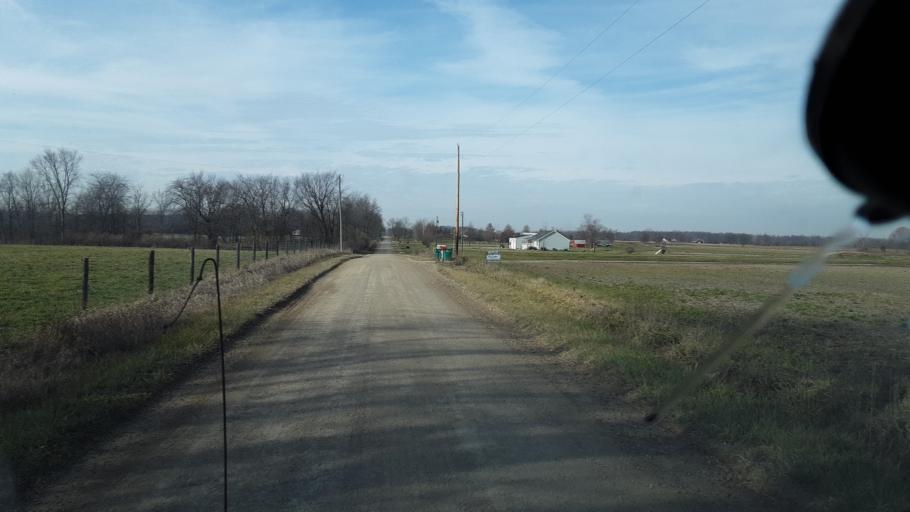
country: US
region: Ohio
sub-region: Defiance County
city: Hicksville
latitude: 41.2703
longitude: -84.8360
